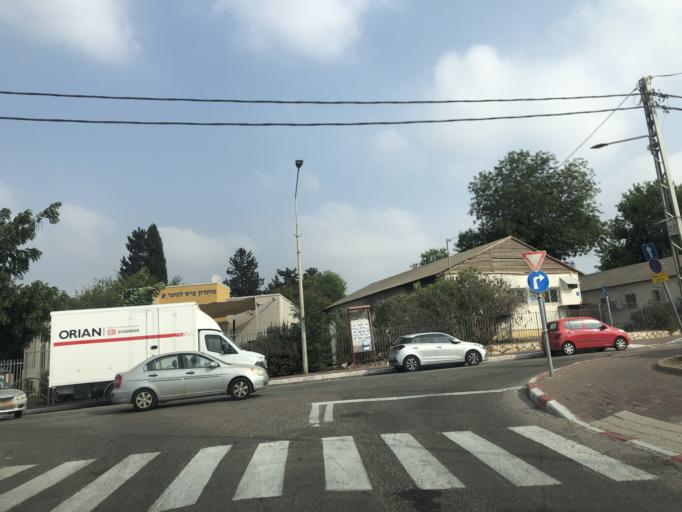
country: IL
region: Central District
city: Rosh Ha'Ayin
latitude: 32.0964
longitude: 34.9502
